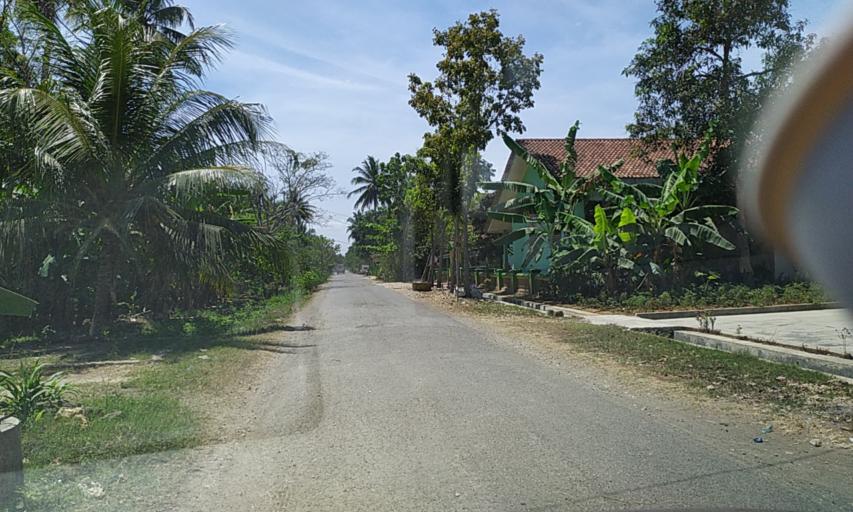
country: ID
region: Central Java
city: Sidaurip
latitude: -7.5571
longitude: 108.7563
